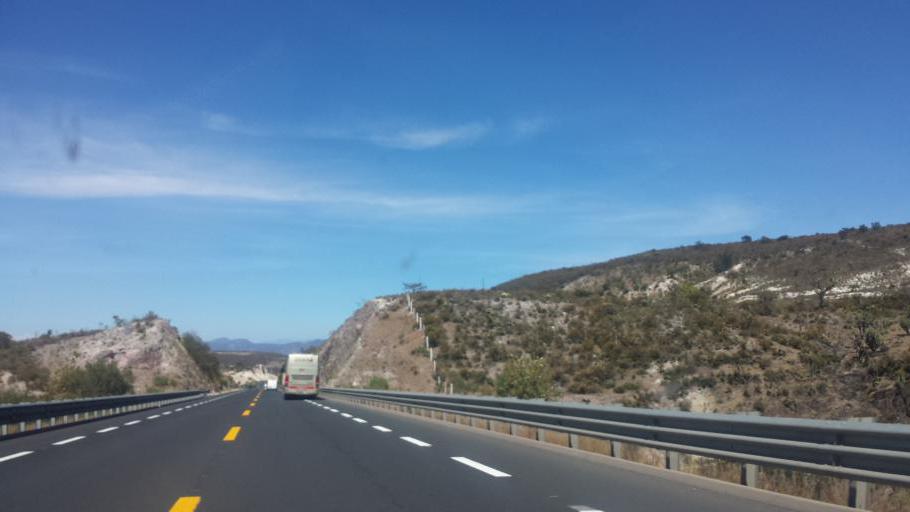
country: MX
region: Oaxaca
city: San Gabriel Casa Blanca
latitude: 17.9544
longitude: -97.3555
